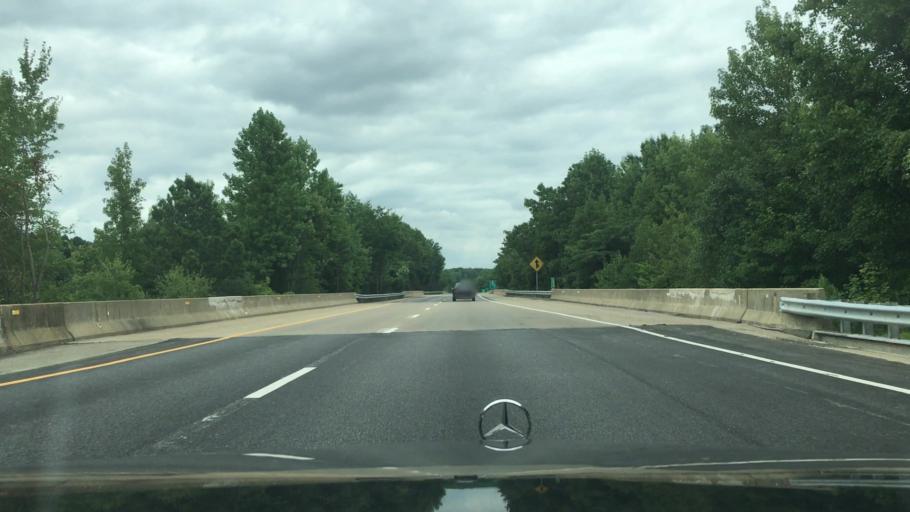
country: US
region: Virginia
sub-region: Chesterfield County
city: Bon Air
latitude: 37.5232
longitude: -77.5314
